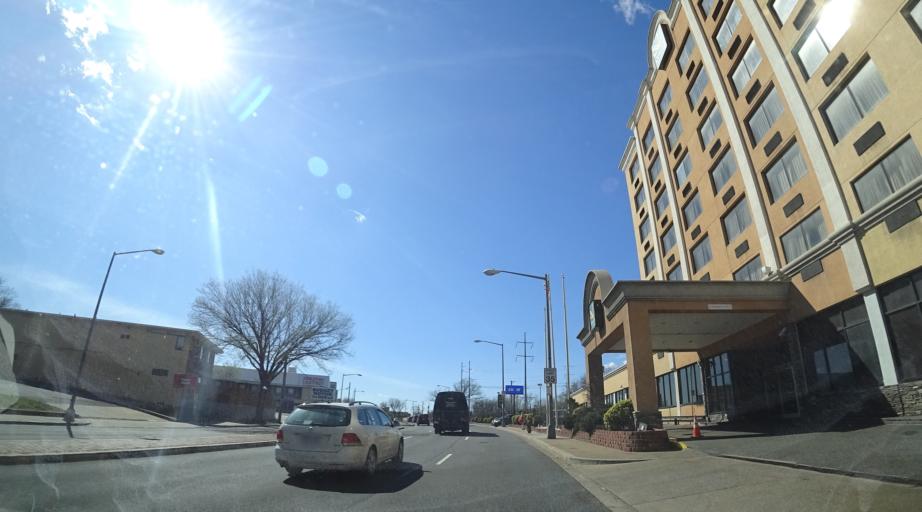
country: US
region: Maryland
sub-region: Prince George's County
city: Mount Rainier
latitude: 38.9174
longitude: -76.9799
